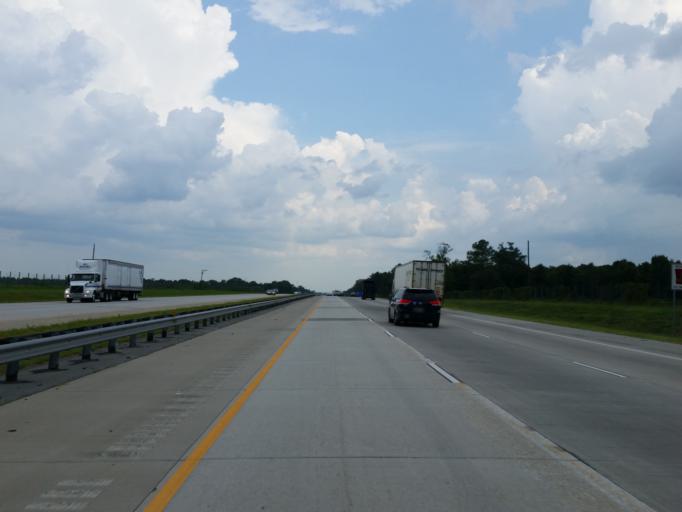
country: US
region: Georgia
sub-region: Dooly County
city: Unadilla
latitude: 32.2840
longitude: -83.7571
